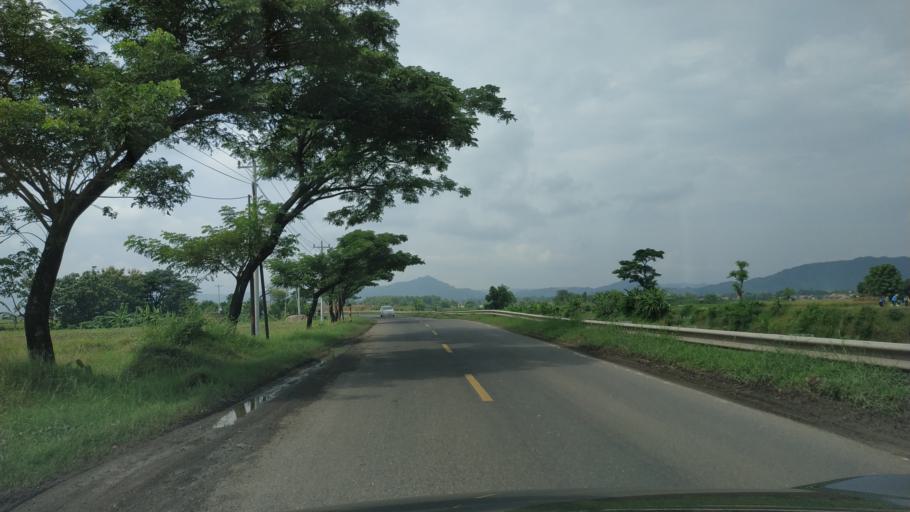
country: ID
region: Central Java
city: Margasari
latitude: -7.0823
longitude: 108.9825
